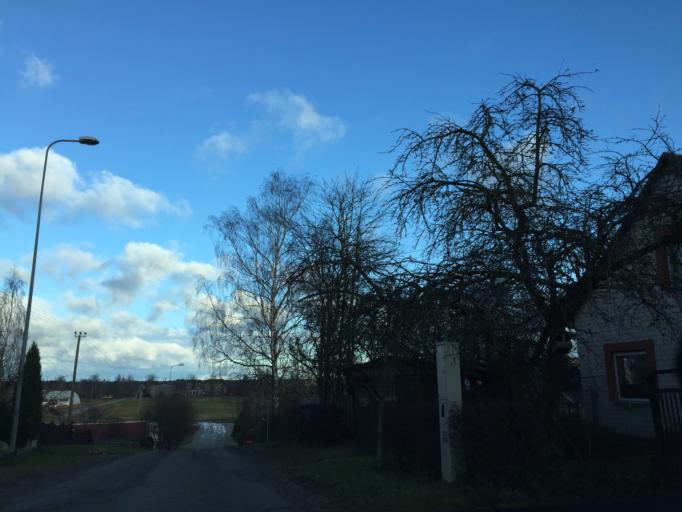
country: LV
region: Valmieras Rajons
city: Valmiera
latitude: 57.5361
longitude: 25.3855
